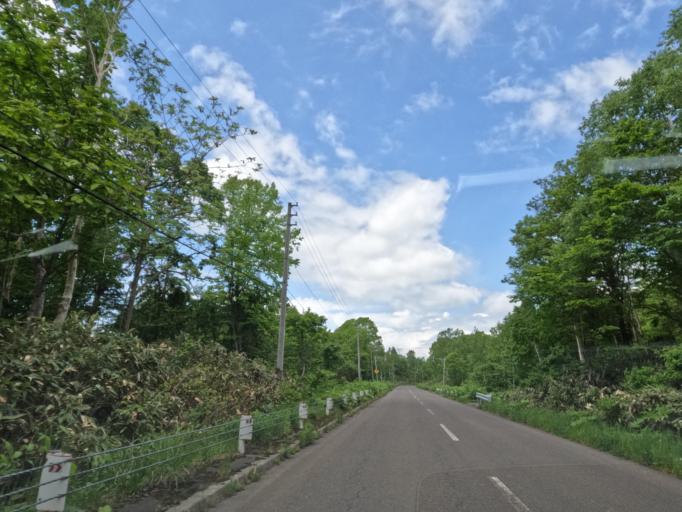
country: JP
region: Hokkaido
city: Tobetsu
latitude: 43.4929
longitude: 141.6062
